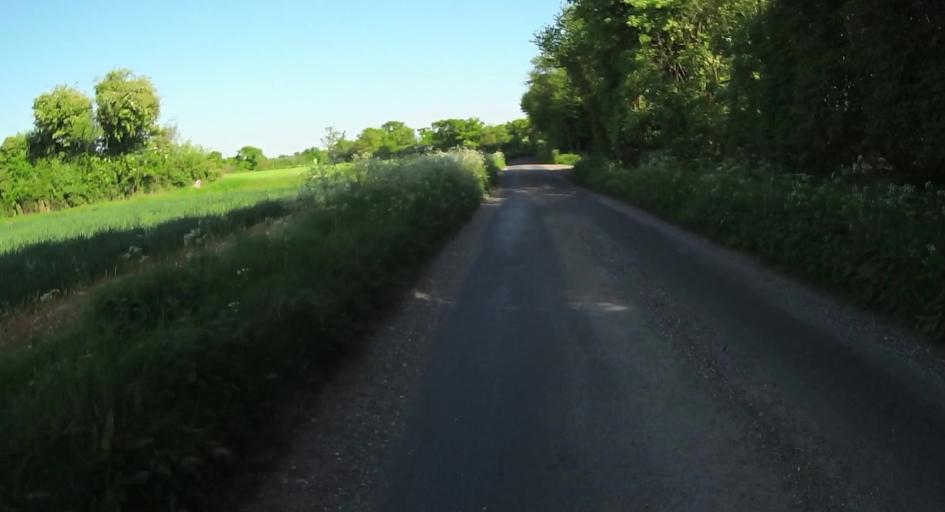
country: GB
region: England
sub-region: Hampshire
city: Overton
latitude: 51.1652
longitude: -1.1871
